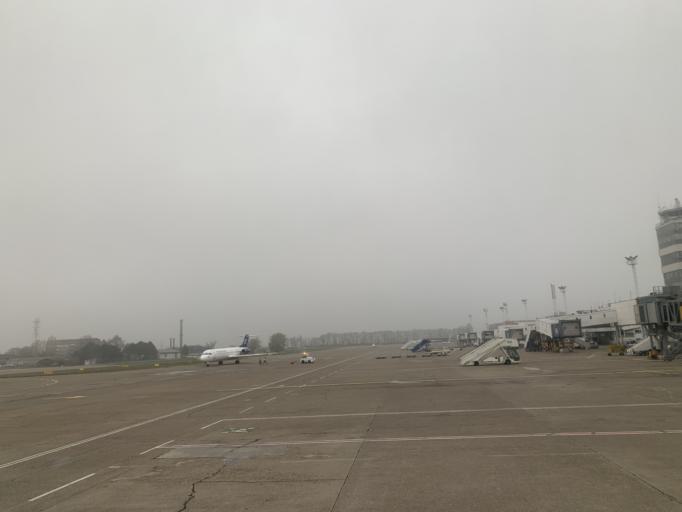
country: RS
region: Central Serbia
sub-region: Belgrade
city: Surcin
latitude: 44.8192
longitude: 20.2929
